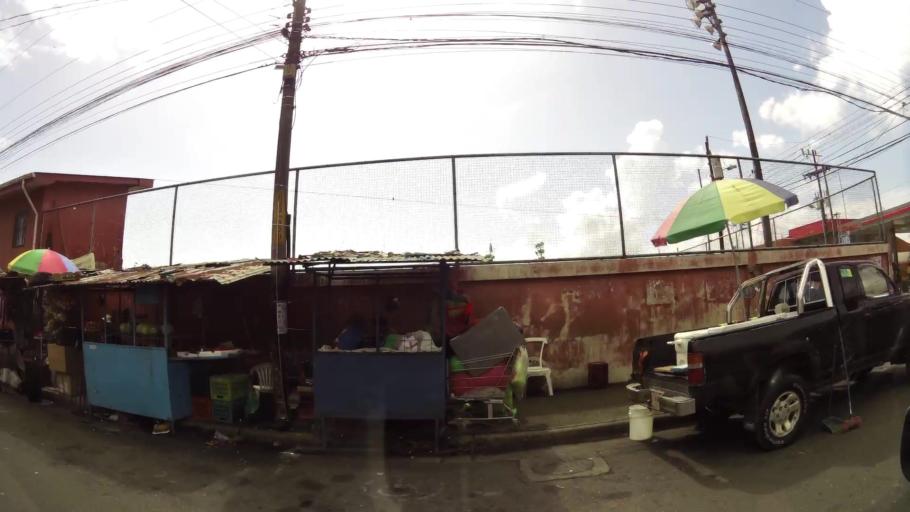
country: CR
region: Limon
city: Limon
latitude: 9.9912
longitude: -83.0316
